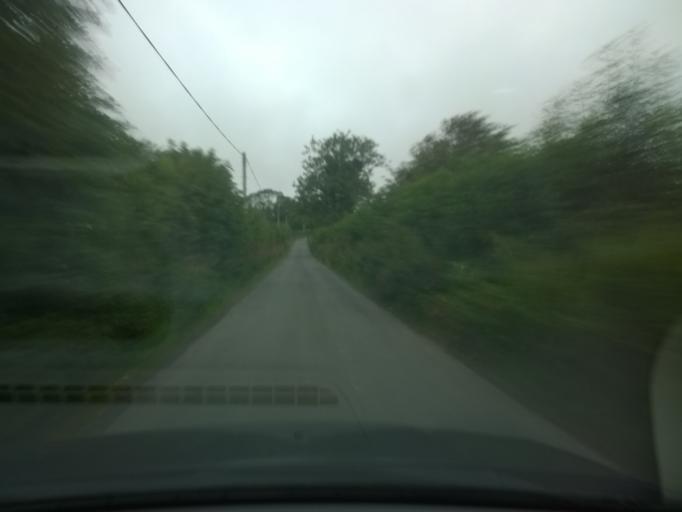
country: IE
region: Leinster
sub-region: Kildare
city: Kildare
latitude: 53.1769
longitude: -6.9398
